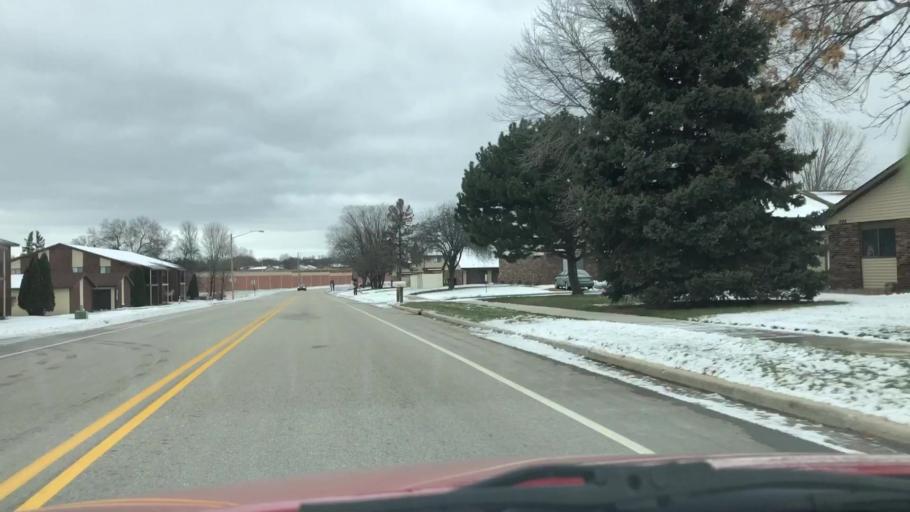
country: US
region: Wisconsin
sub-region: Brown County
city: Ashwaubenon
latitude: 44.4864
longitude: -88.0787
